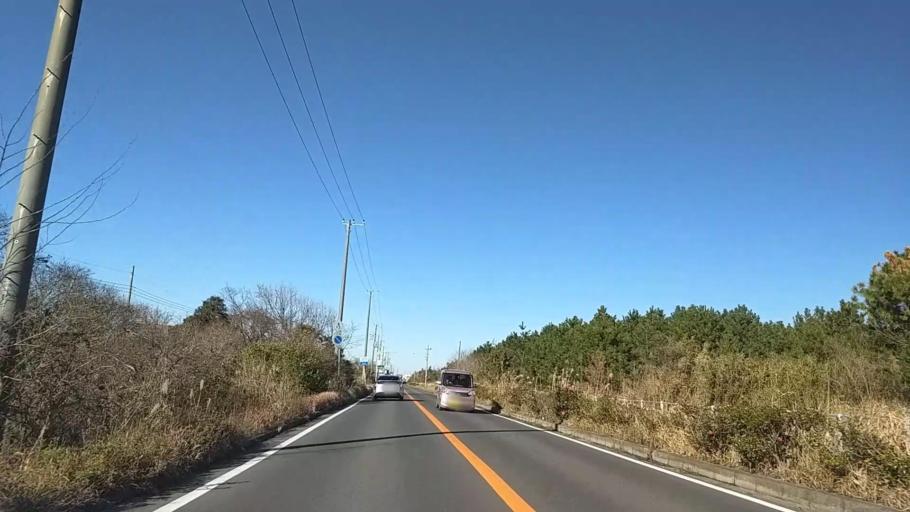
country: JP
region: Chiba
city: Ohara
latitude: 35.3367
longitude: 140.3914
